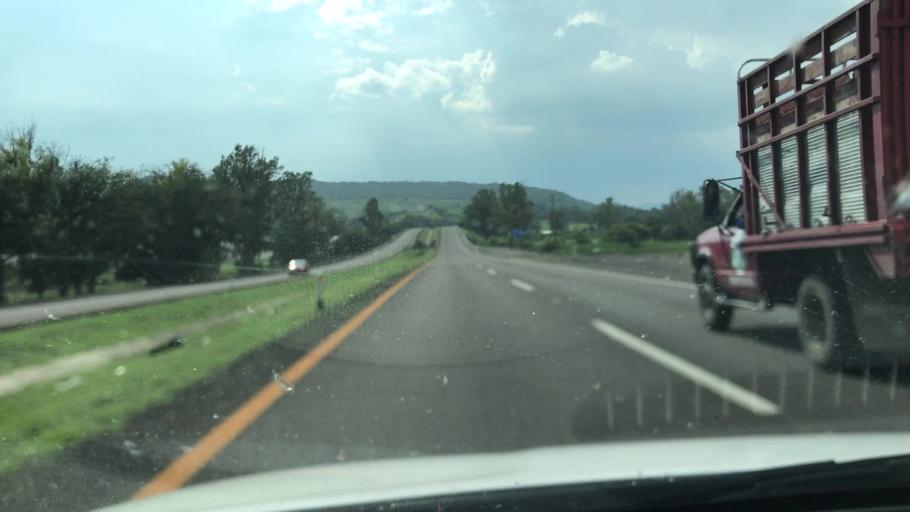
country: MX
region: Jalisco
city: Ocotlan
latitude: 20.3959
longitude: -102.7261
